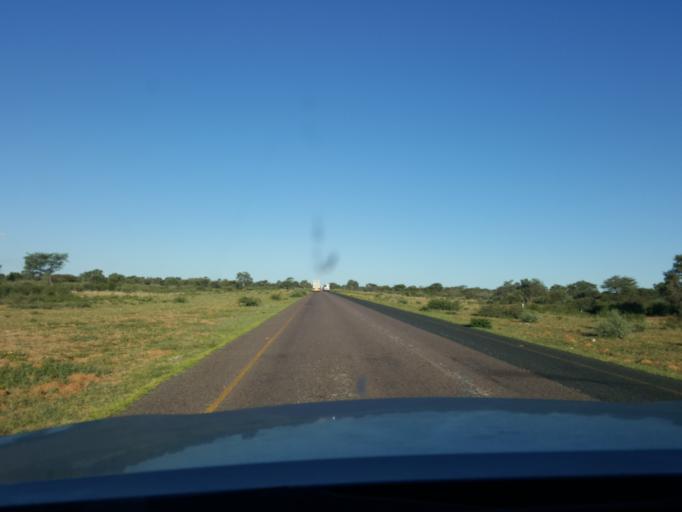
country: BW
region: Southern
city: Khakhea
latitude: -24.2607
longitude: 23.3148
